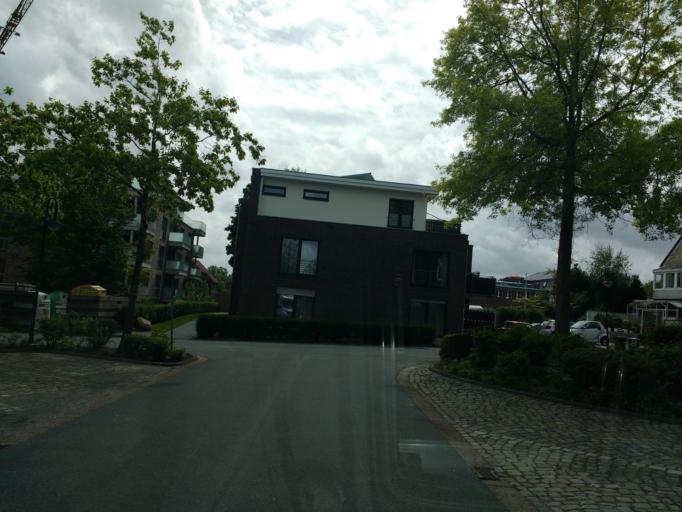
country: DE
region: Lower Saxony
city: Jever
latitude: 53.5727
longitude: 7.9068
